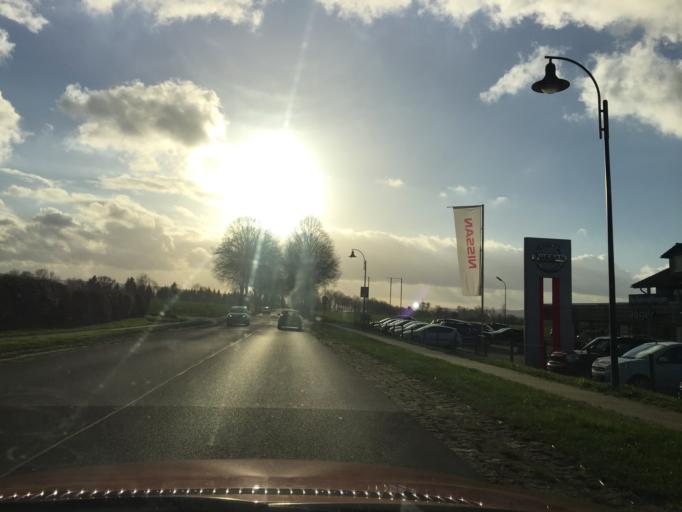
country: DE
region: Lower Saxony
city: Bevern
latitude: 51.8528
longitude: 9.4895
